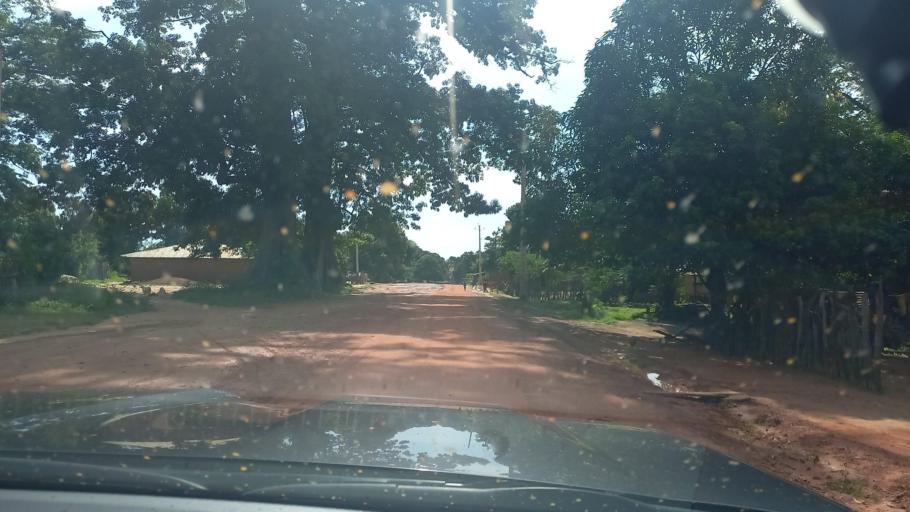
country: SN
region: Ziguinchor
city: Ziguinchor
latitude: 12.6753
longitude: -16.1956
